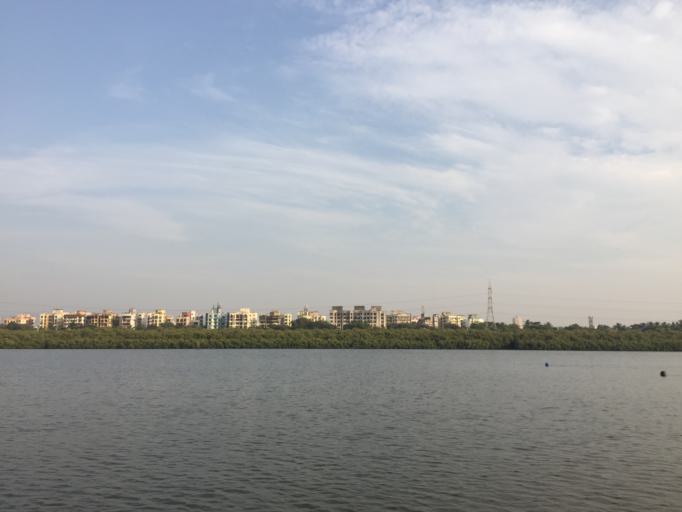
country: IN
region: Maharashtra
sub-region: Mumbai Suburban
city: Borivli
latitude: 19.2312
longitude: 72.8183
